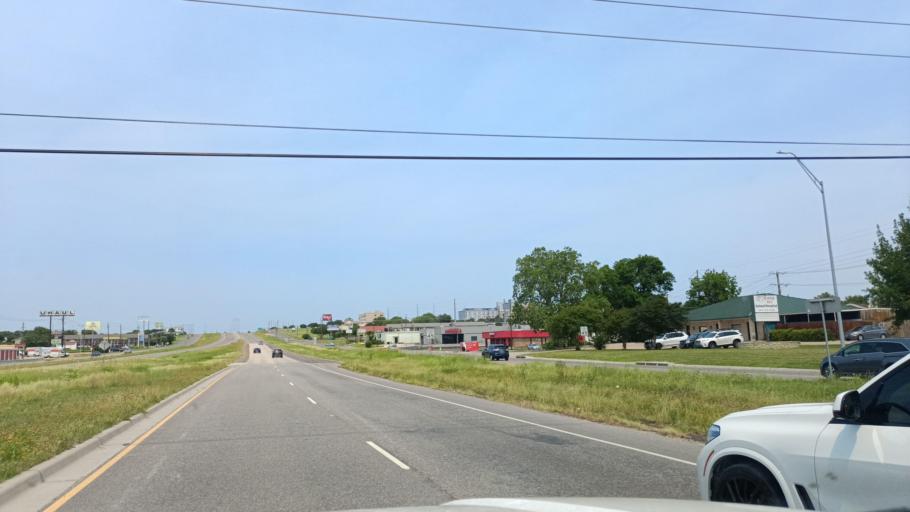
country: US
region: Texas
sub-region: Bell County
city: Temple
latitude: 31.0701
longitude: -97.3546
